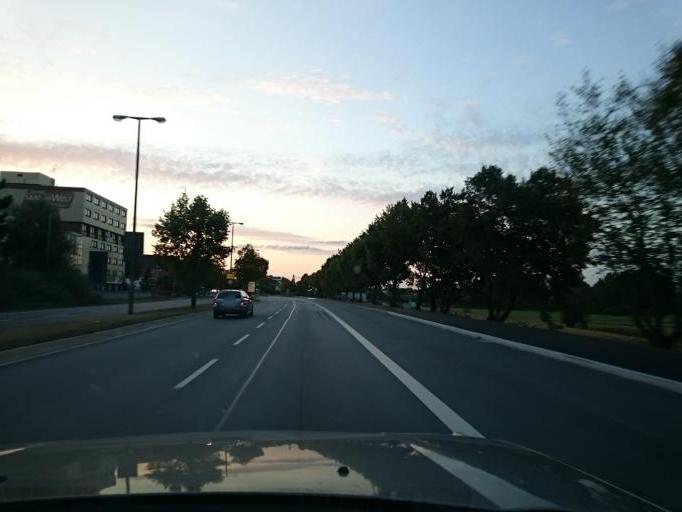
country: DE
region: Bavaria
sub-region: Upper Palatinate
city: Regensburg
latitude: 48.9980
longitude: 12.1321
